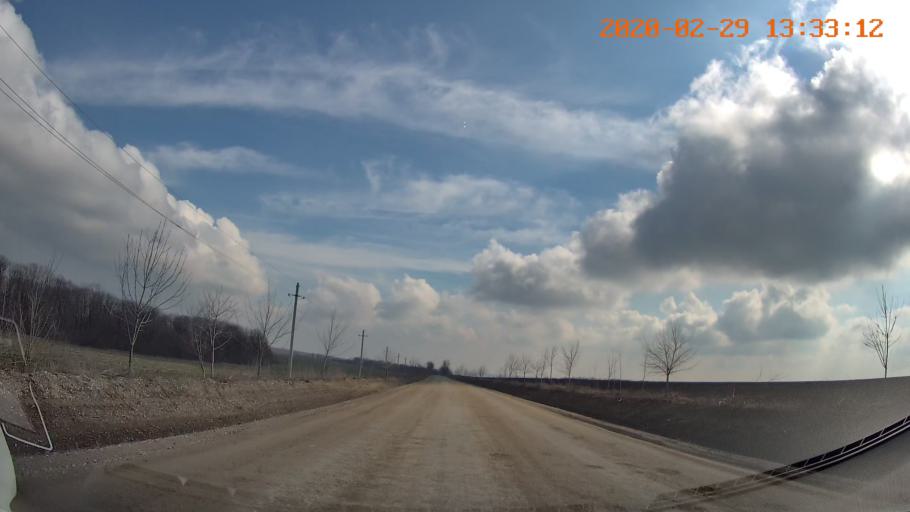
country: MD
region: Telenesti
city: Camenca
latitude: 47.8749
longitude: 28.6147
